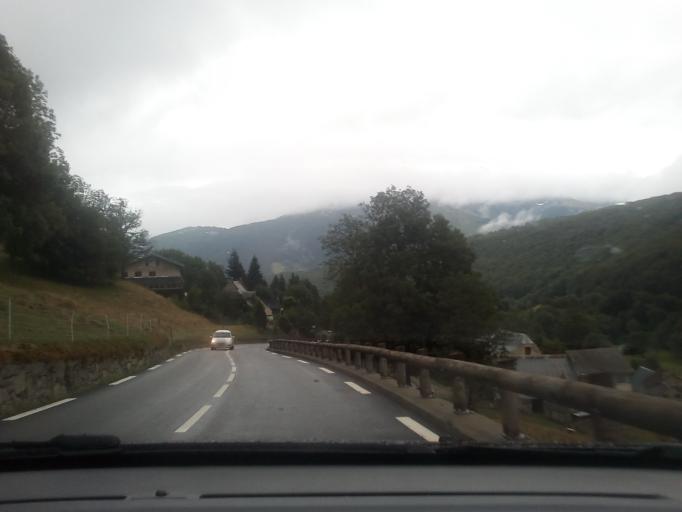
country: FR
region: Midi-Pyrenees
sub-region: Departement des Hautes-Pyrenees
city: Campan
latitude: 42.9445
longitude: 0.2197
